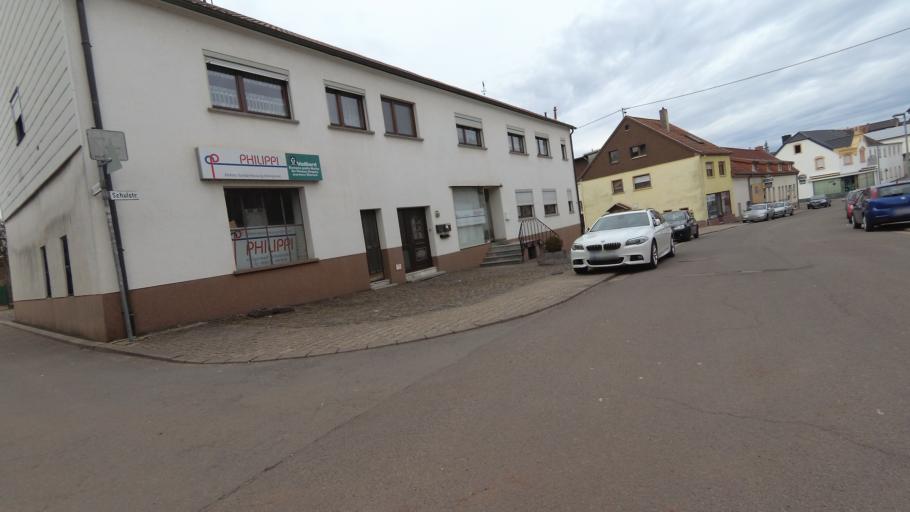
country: DE
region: Saarland
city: Friedrichsthal
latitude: 49.3548
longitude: 7.0976
